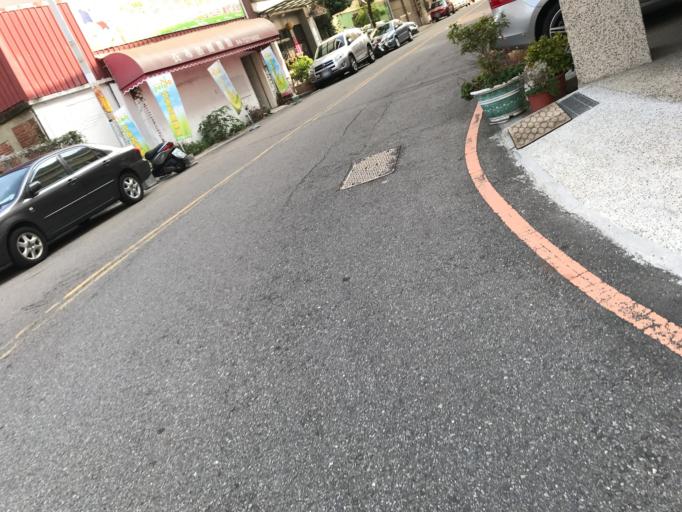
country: TW
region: Taiwan
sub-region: Changhua
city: Chang-hua
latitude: 24.0850
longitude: 120.5514
